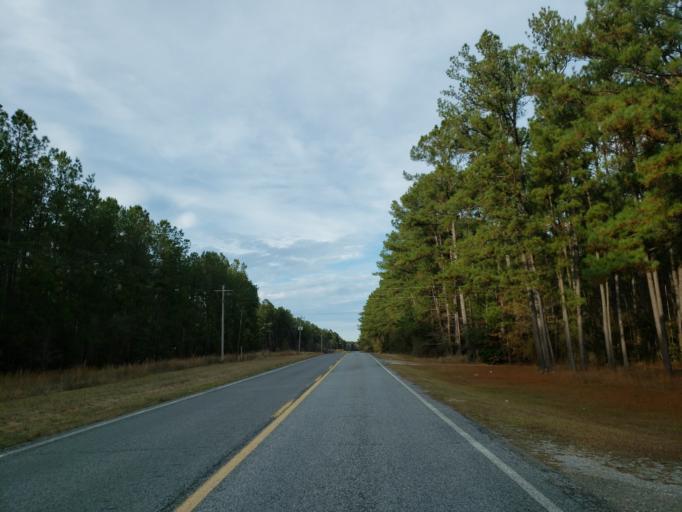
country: US
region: Mississippi
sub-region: Wayne County
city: Waynesboro
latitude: 31.8295
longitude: -88.6900
